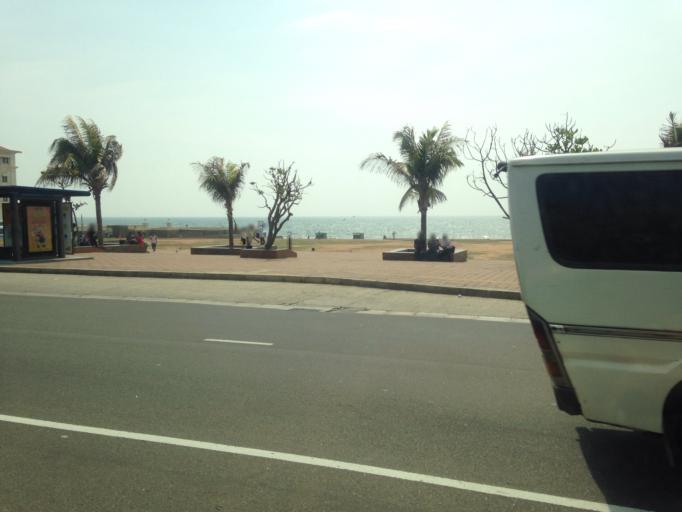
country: LK
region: Western
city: Colombo
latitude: 6.9218
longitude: 79.8462
